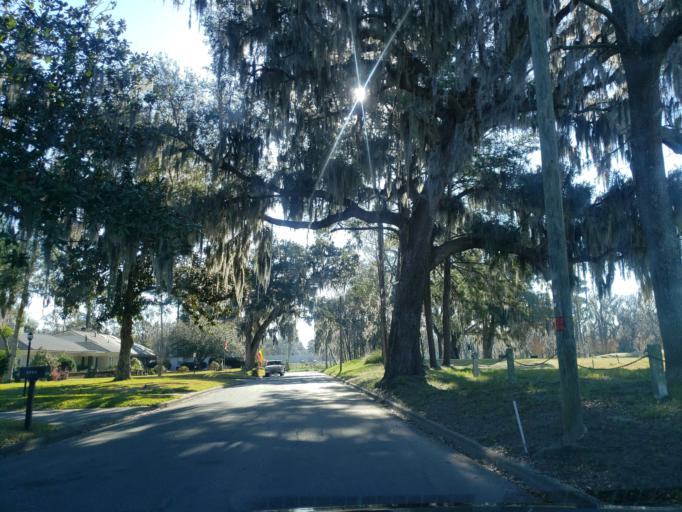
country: US
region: Georgia
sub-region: Chatham County
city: Thunderbolt
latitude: 32.0172
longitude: -81.0893
